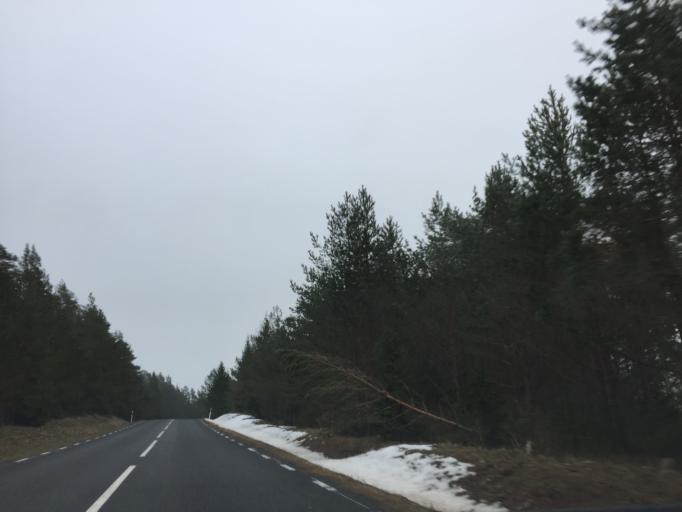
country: EE
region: Saare
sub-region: Kuressaare linn
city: Kuressaare
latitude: 58.4657
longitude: 22.0426
